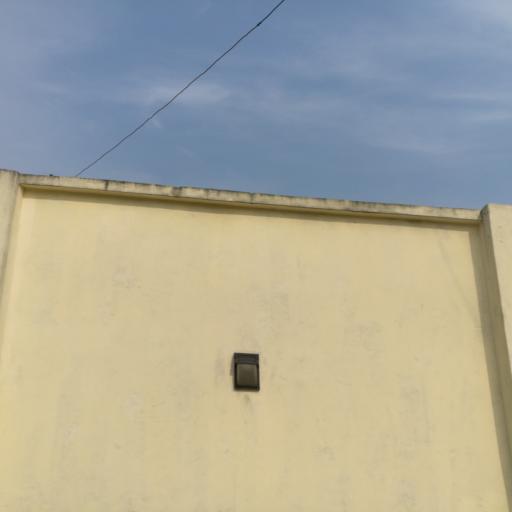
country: NG
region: Rivers
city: Port Harcourt
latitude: 4.8449
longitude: 7.0491
